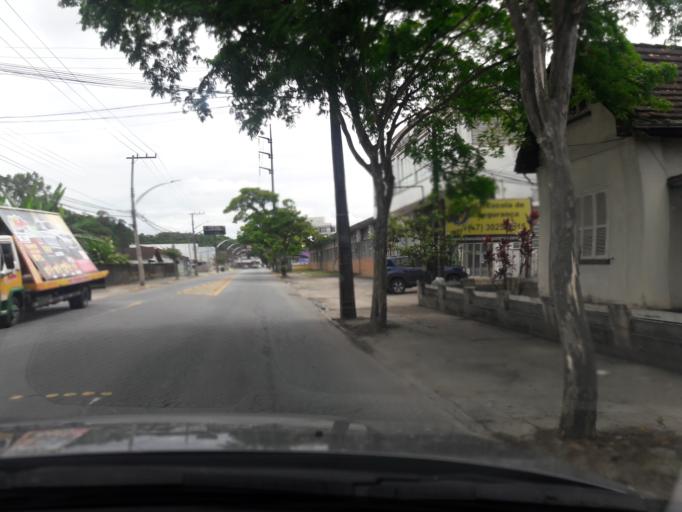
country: BR
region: Santa Catarina
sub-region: Joinville
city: Joinville
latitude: -26.3221
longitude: -48.8536
